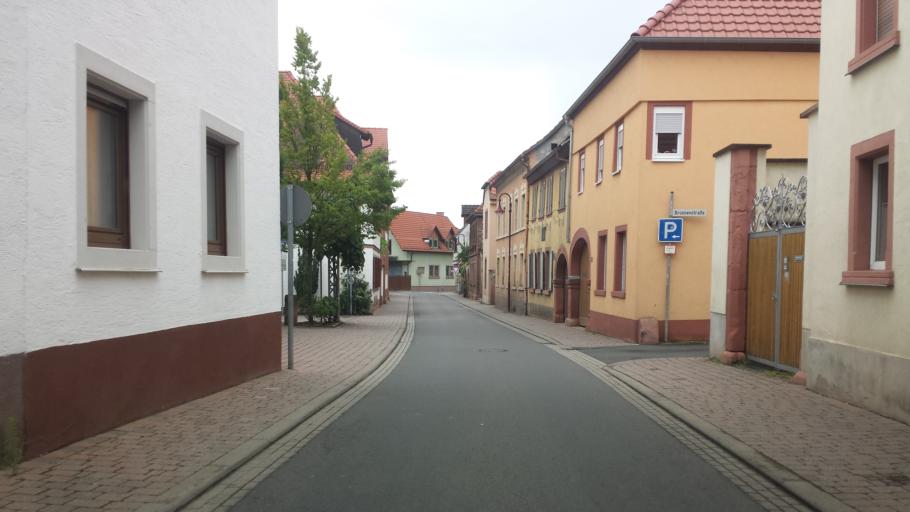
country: DE
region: Rheinland-Pfalz
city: Maikammer
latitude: 49.3036
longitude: 8.1306
